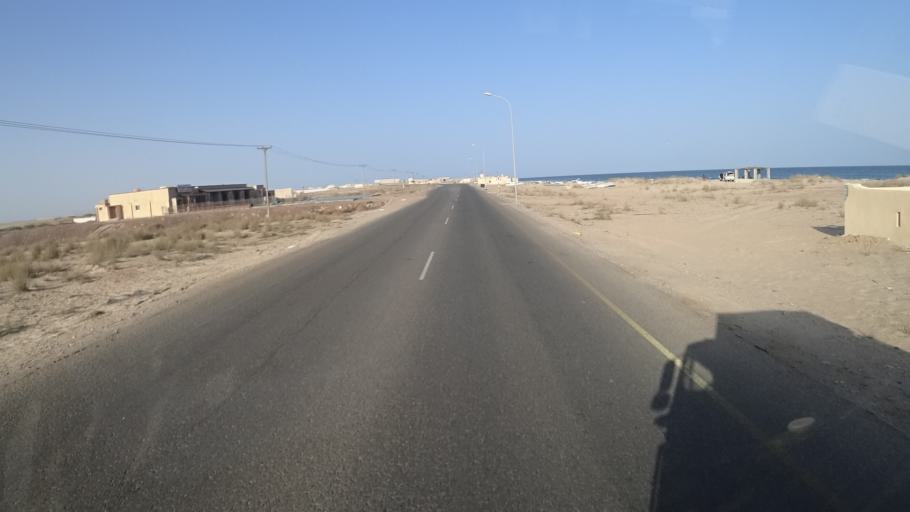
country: OM
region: Ash Sharqiyah
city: Sur
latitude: 22.1651
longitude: 59.7544
